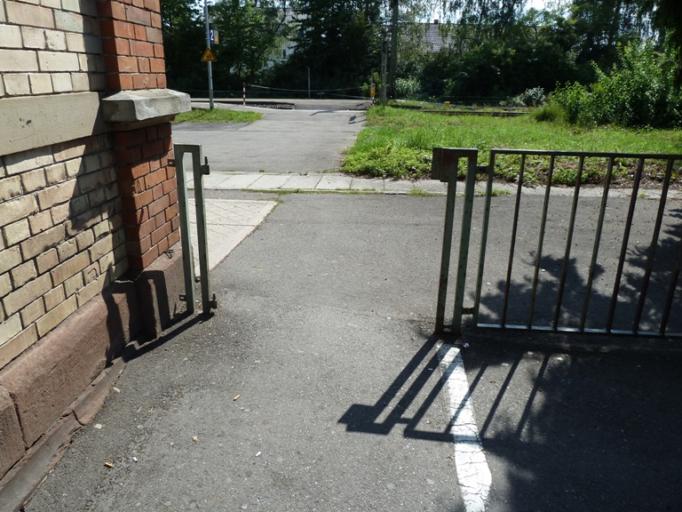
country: DE
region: Baden-Wuerttemberg
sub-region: Tuebingen Region
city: Markdorf
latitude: 47.7170
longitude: 9.3885
